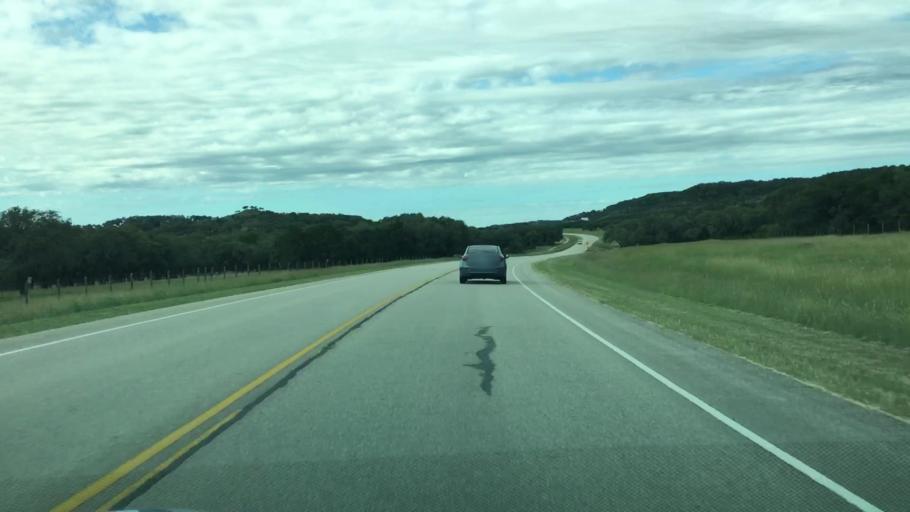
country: US
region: Texas
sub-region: Hays County
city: Wimberley
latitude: 30.0104
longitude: -98.0839
